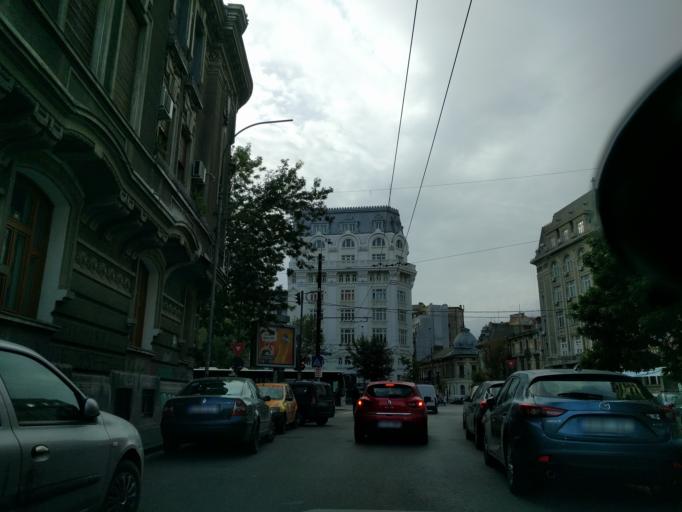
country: RO
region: Bucuresti
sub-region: Municipiul Bucuresti
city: Bucharest
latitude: 44.4366
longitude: 26.1059
